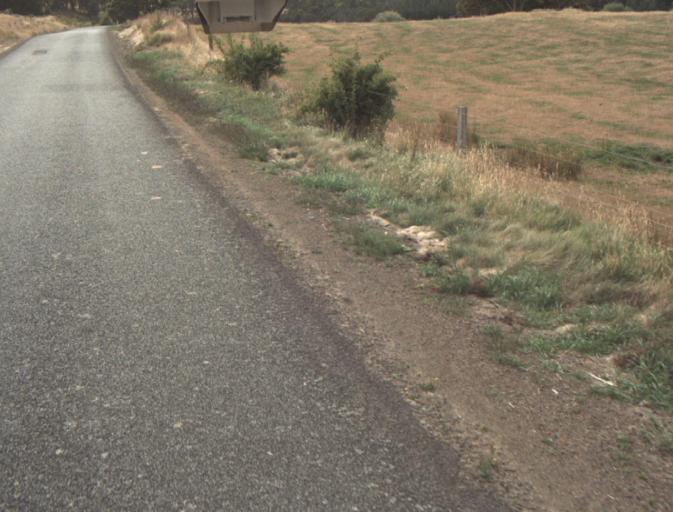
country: AU
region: Tasmania
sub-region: Dorset
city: Scottsdale
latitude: -41.4663
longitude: 147.5875
